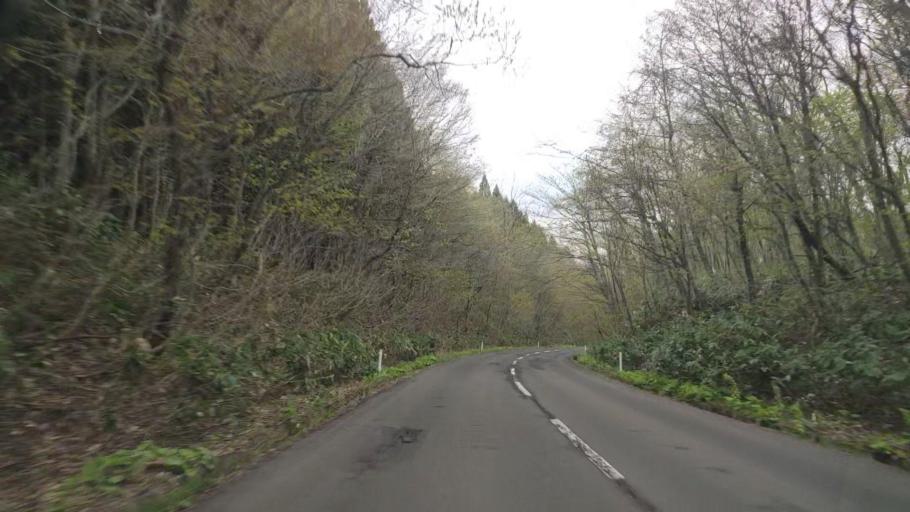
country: JP
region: Akita
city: Hanawa
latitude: 40.3846
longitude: 140.7924
